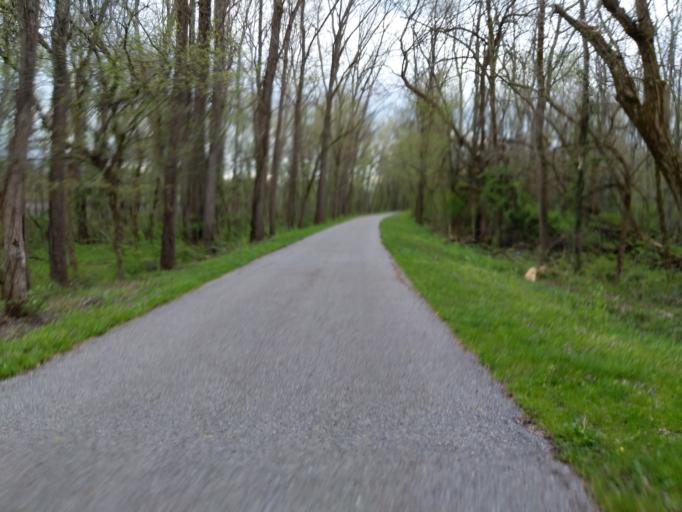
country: US
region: Ohio
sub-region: Athens County
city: Chauncey
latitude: 39.3822
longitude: -82.1155
